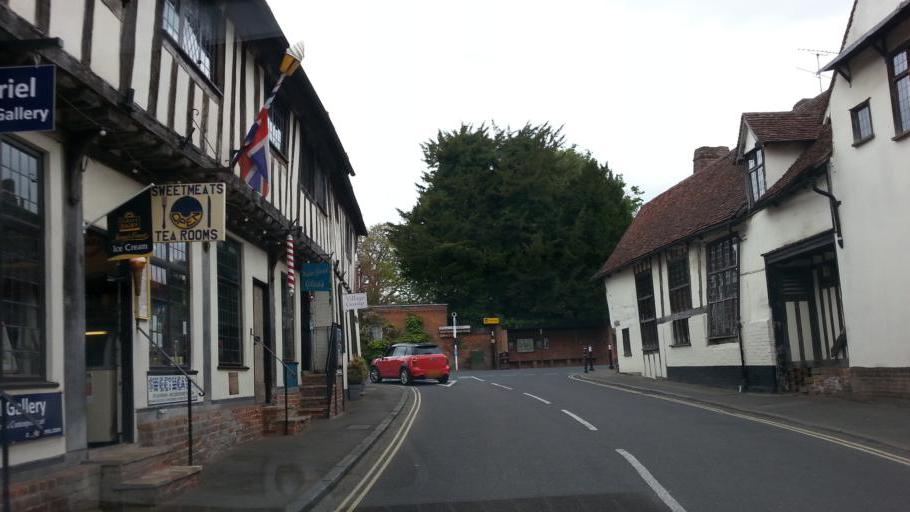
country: GB
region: England
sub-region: Suffolk
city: Lavenham
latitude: 52.1076
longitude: 0.7960
